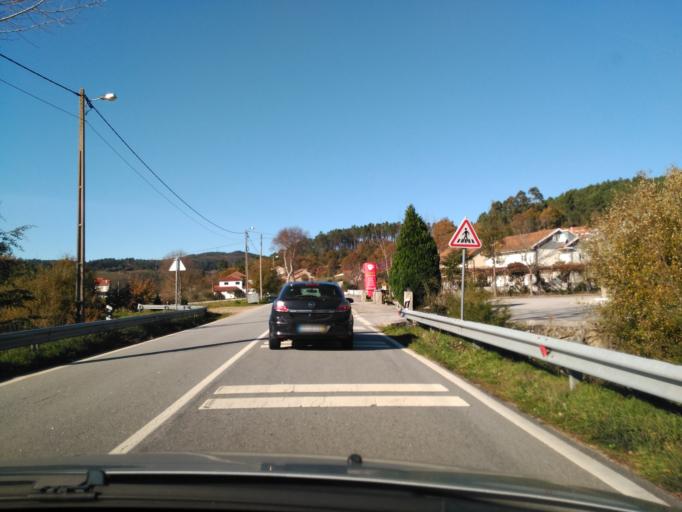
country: PT
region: Braga
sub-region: Cabeceiras de Basto
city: Cabeceiras de Basto
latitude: 41.6805
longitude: -7.9504
